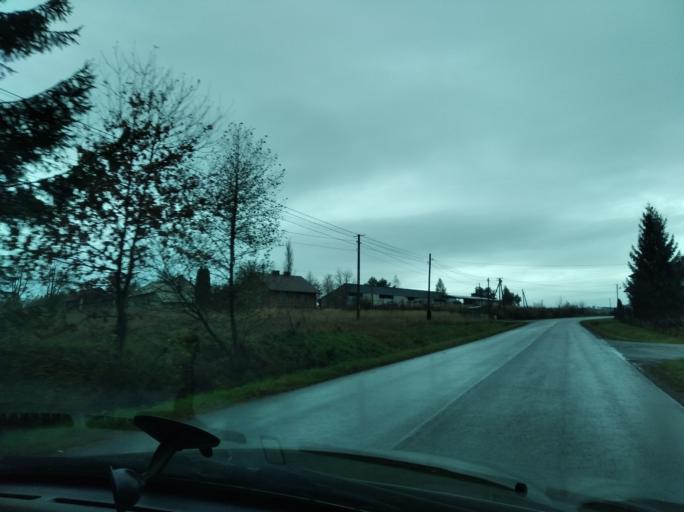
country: PL
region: Subcarpathian Voivodeship
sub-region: Powiat rzeszowski
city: Lecka
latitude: 49.9095
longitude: 22.0218
